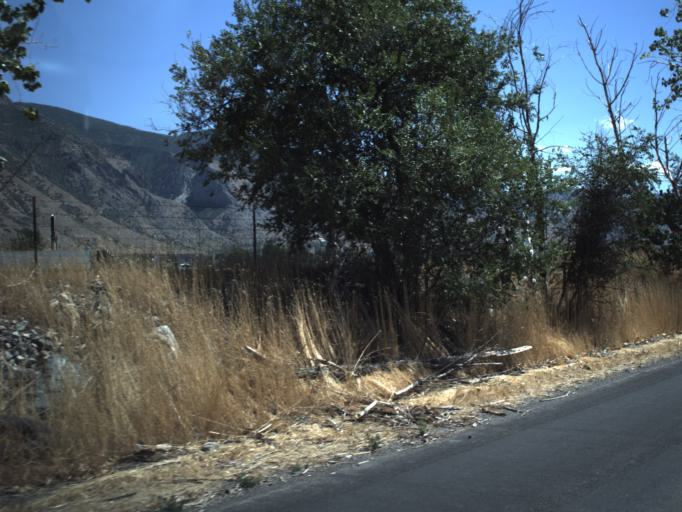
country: US
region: Utah
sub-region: Utah County
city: Springville
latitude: 40.1866
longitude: -111.6484
